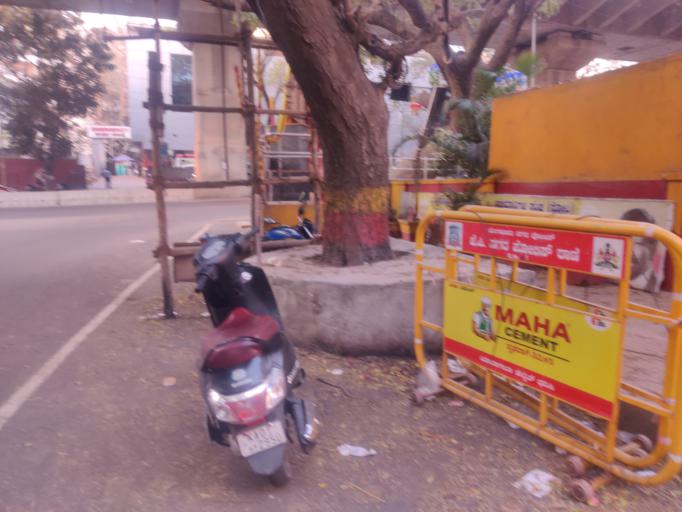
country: IN
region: Karnataka
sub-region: Bangalore Urban
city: Bangalore
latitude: 12.9166
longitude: 77.5916
